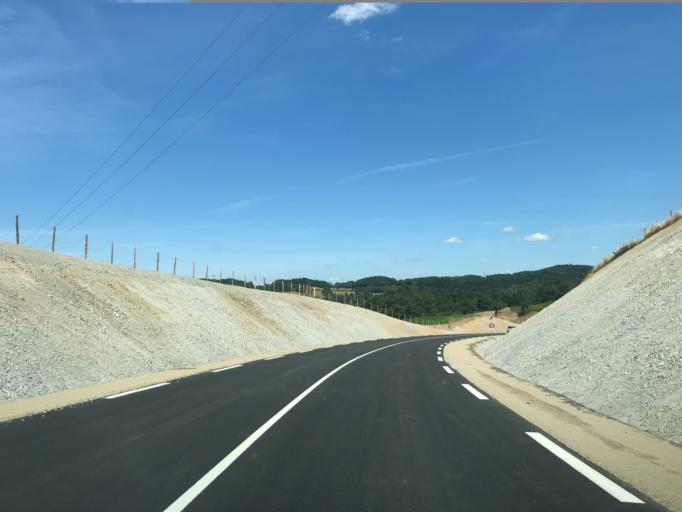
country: FR
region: Limousin
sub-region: Departement de la Creuse
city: Aubusson
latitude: 45.9451
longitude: 2.1930
